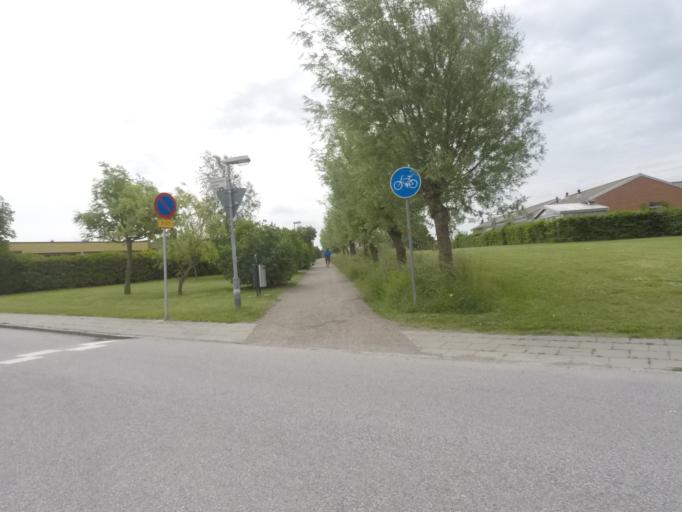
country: SE
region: Skane
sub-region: Malmo
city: Tygelsjo
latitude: 55.5189
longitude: 12.9927
